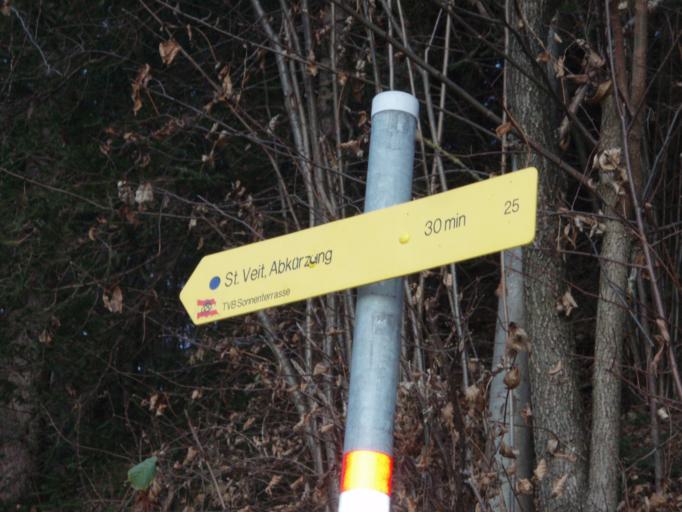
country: AT
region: Salzburg
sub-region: Politischer Bezirk Sankt Johann im Pongau
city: Schwarzach im Pongau
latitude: 47.3230
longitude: 13.1534
